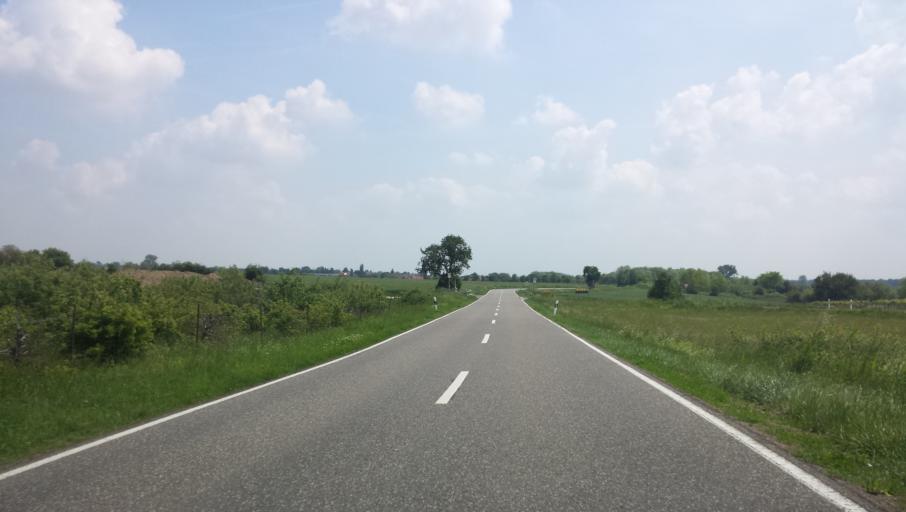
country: DE
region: Rheinland-Pfalz
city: Schweighofen
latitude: 49.0377
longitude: 7.9753
